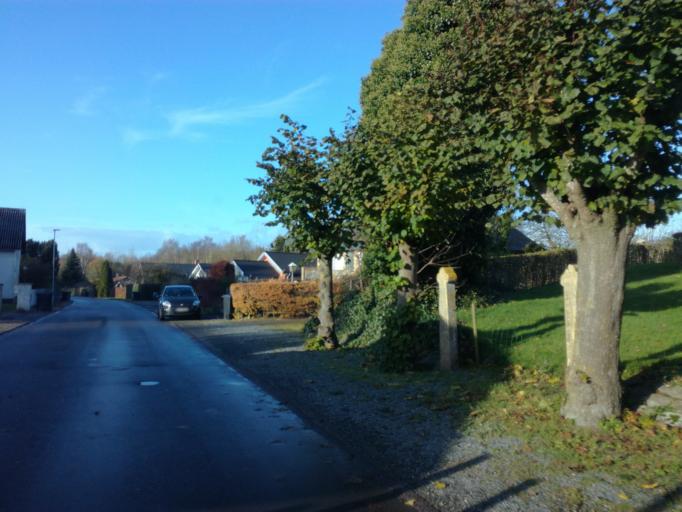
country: DK
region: South Denmark
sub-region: Vejle Kommune
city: Borkop
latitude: 55.6392
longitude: 9.6674
